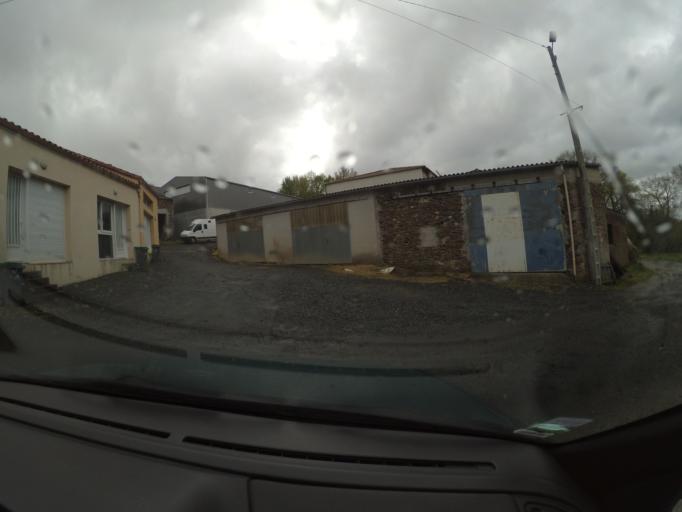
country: FR
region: Pays de la Loire
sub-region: Departement de la Loire-Atlantique
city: Monnieres
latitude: 47.1373
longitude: -1.3456
